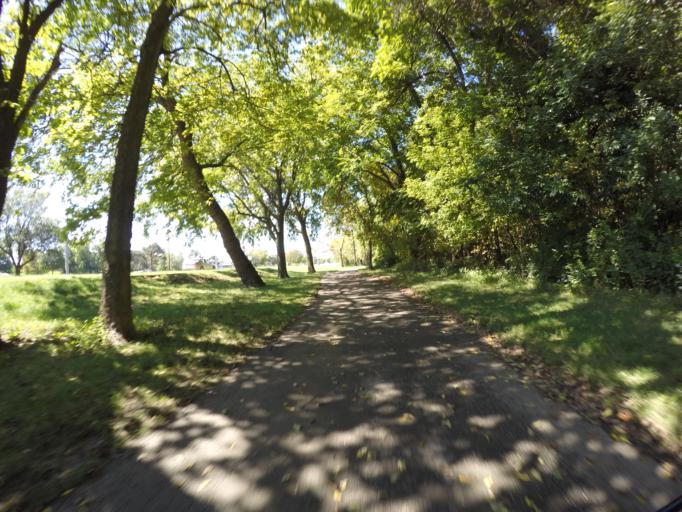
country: US
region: Kansas
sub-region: Johnson County
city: Overland Park
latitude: 38.9423
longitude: -94.6639
